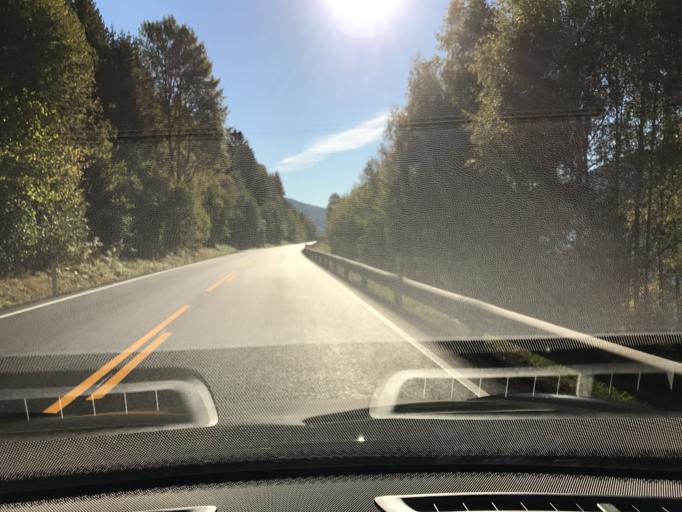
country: NO
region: Buskerud
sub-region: Krodsherad
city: Noresund
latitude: 60.3181
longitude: 9.6745
